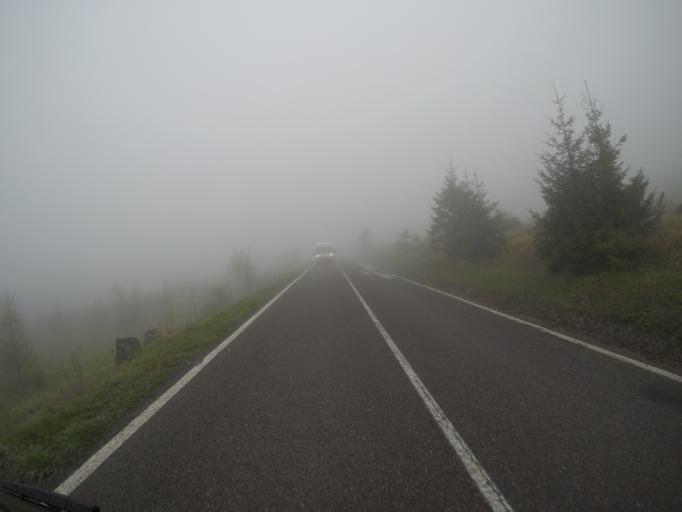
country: SK
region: Presovsky
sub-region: Okres Poprad
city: Strba
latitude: 49.1099
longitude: 20.0690
